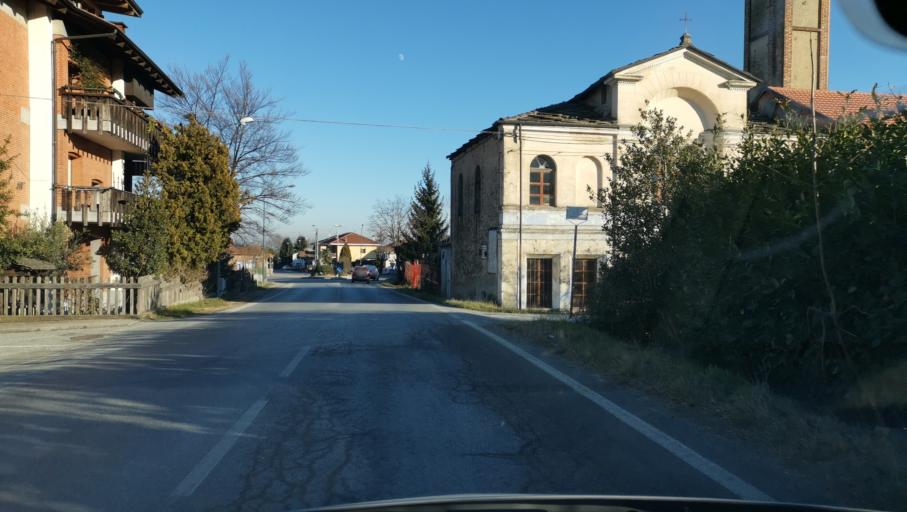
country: IT
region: Piedmont
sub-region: Provincia di Cuneo
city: Bagnolo Piemonte
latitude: 44.7573
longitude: 7.3125
